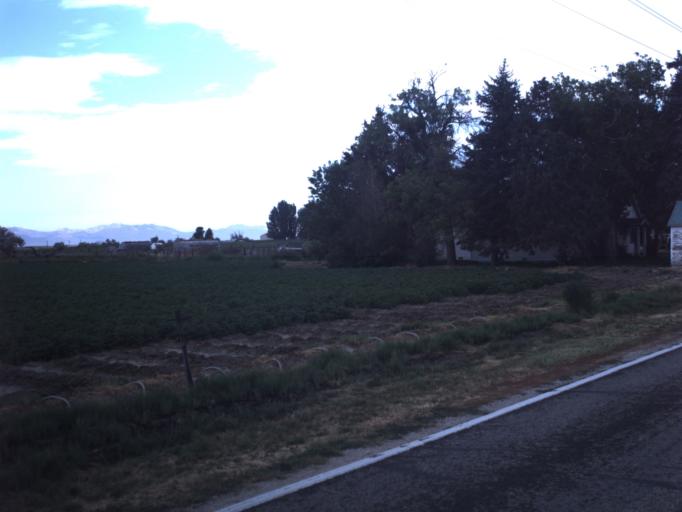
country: US
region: Utah
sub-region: Davis County
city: West Point
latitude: 41.0994
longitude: -112.1127
